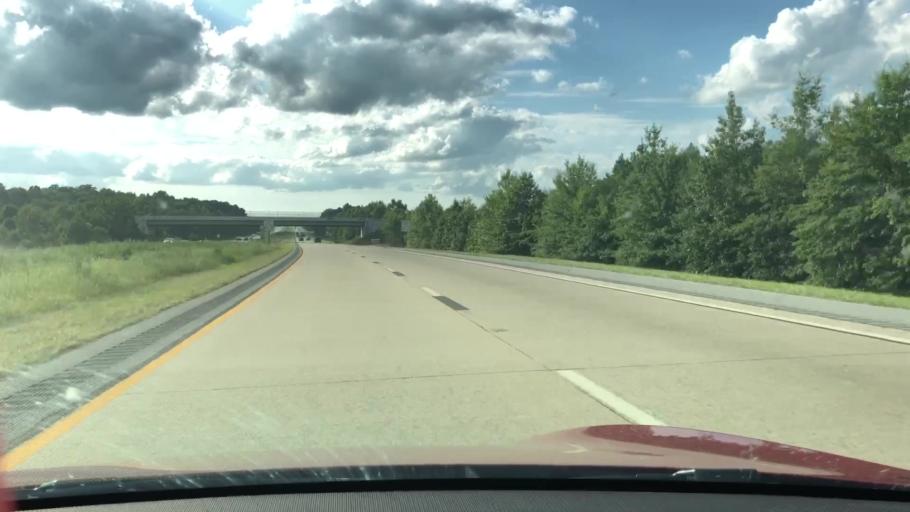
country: US
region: Delaware
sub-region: Kent County
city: Smyrna
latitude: 39.3211
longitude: -75.6071
